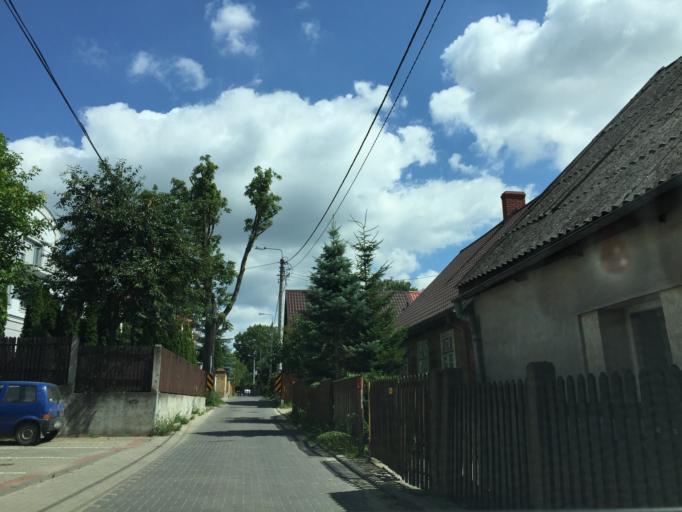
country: PL
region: Podlasie
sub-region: Bialystok
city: Bialystok
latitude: 53.1341
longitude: 23.1781
